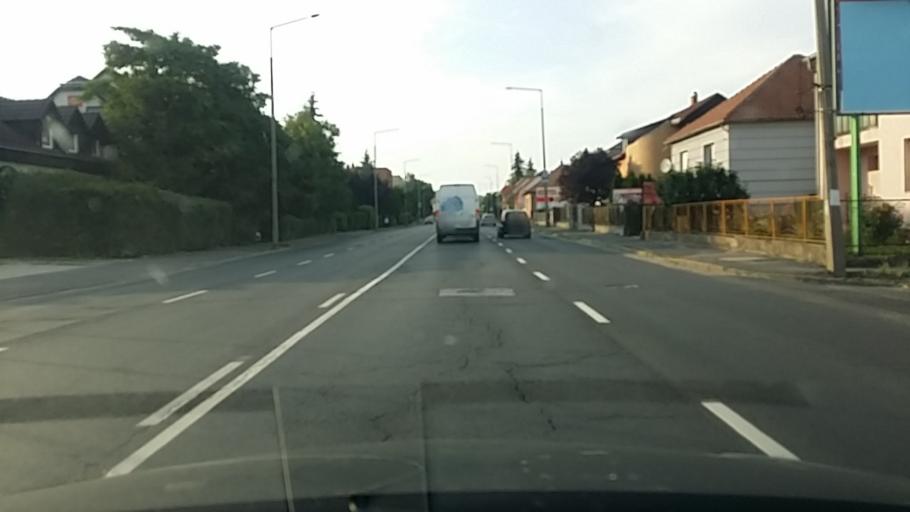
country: HU
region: Borsod-Abauj-Zemplen
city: Miskolc
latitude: 48.0695
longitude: 20.7908
